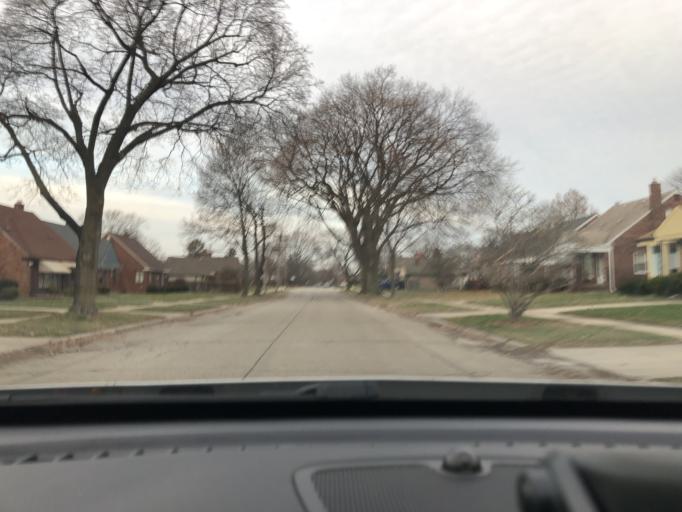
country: US
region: Michigan
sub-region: Wayne County
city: Allen Park
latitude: 42.2880
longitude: -83.2203
